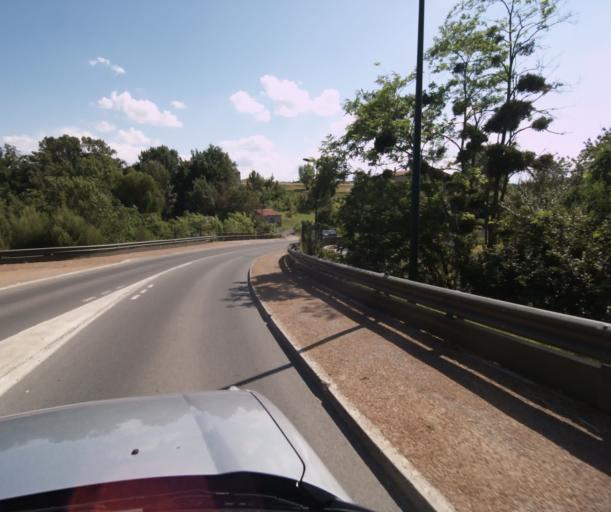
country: FR
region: Languedoc-Roussillon
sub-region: Departement de l'Aude
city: Limoux
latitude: 43.0653
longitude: 2.2265
